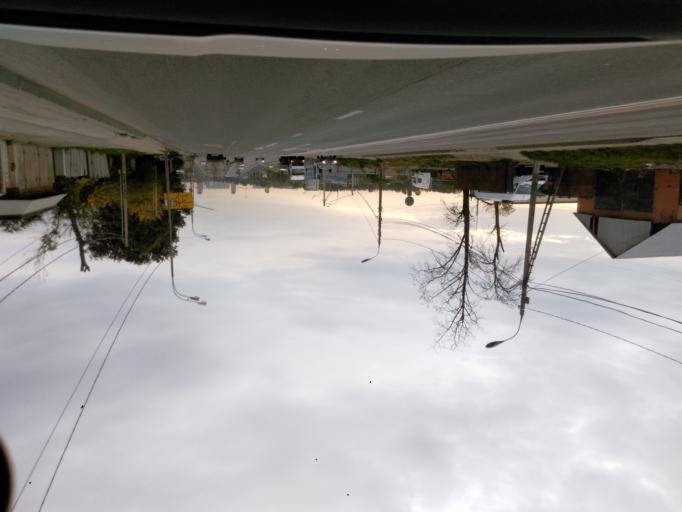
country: RU
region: Moscow
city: Severnyy
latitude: 55.9549
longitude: 37.5360
